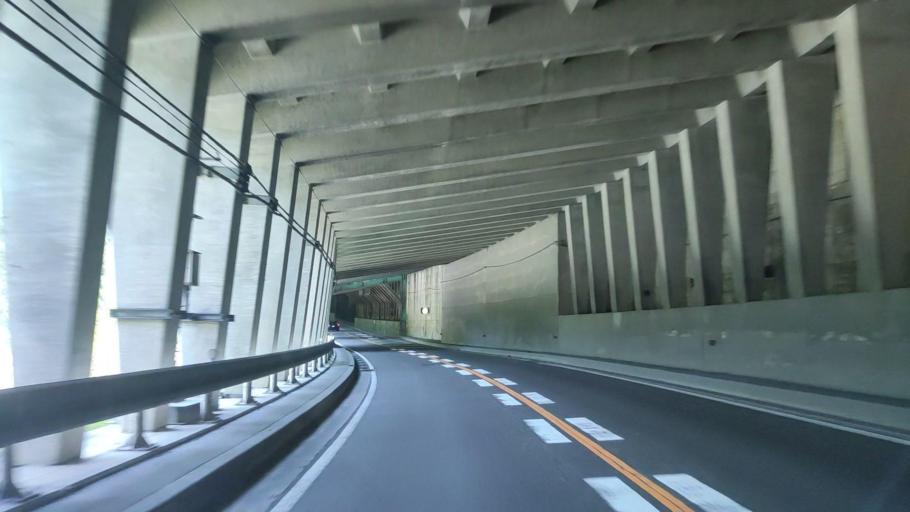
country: JP
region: Niigata
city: Itoigawa
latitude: 36.9068
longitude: 137.8620
